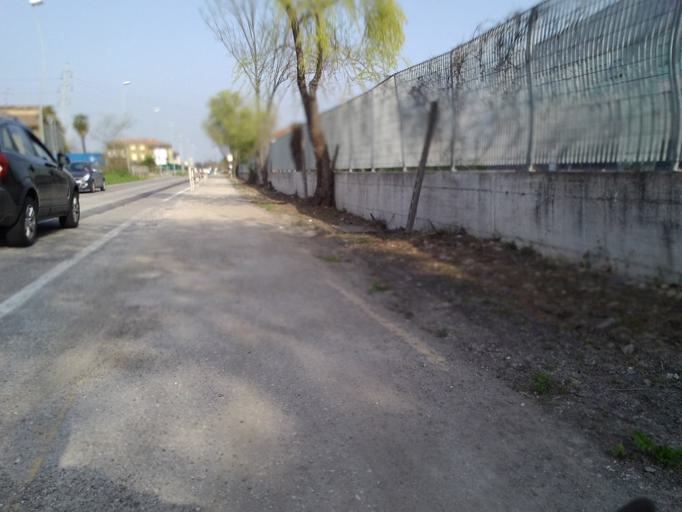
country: IT
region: Veneto
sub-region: Provincia di Verona
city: Dossobuono
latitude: 45.4197
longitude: 10.9348
